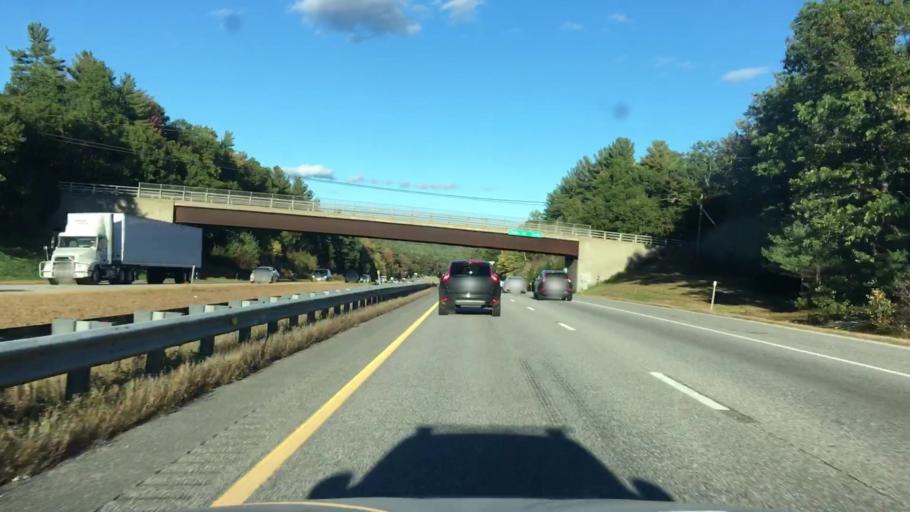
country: US
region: New Hampshire
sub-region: Rockingham County
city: Auburn
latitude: 43.0335
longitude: -71.3408
